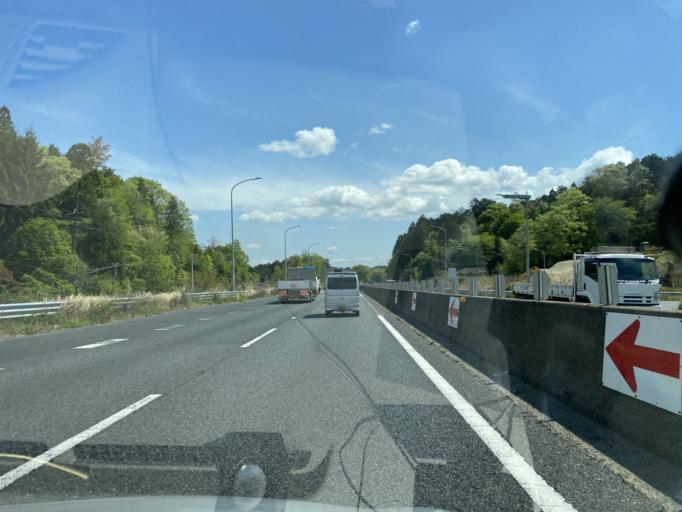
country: JP
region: Mie
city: Nabari
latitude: 34.6502
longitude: 136.0180
